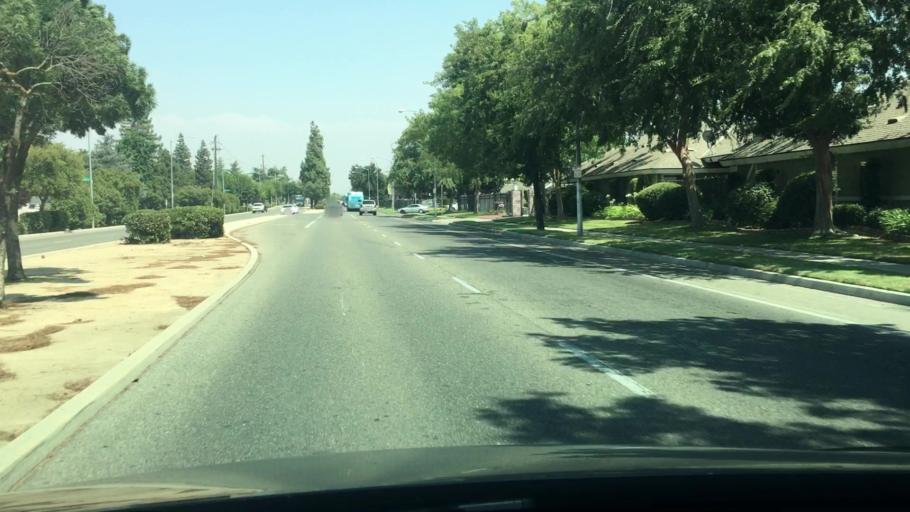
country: US
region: California
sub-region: Fresno County
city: Clovis
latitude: 36.8519
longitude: -119.7806
